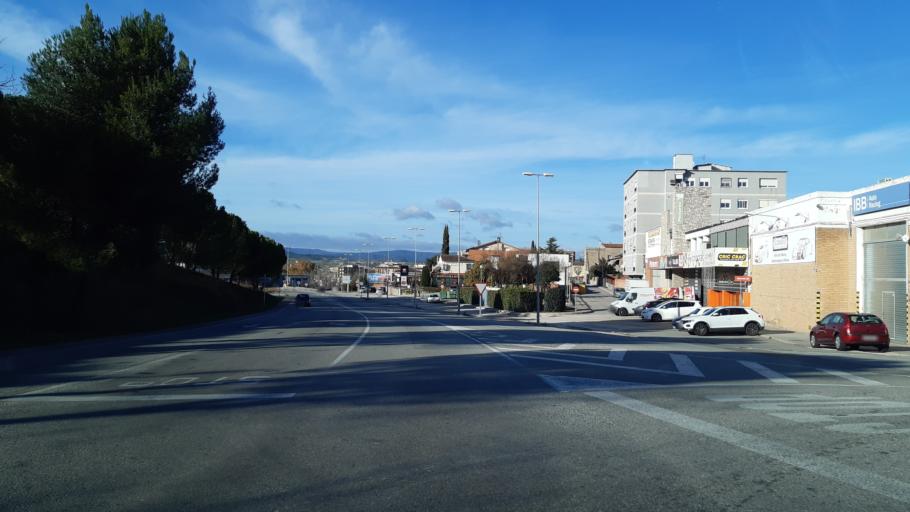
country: ES
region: Catalonia
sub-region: Provincia de Barcelona
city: Vilanova del Cami
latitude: 41.5788
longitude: 1.6426
